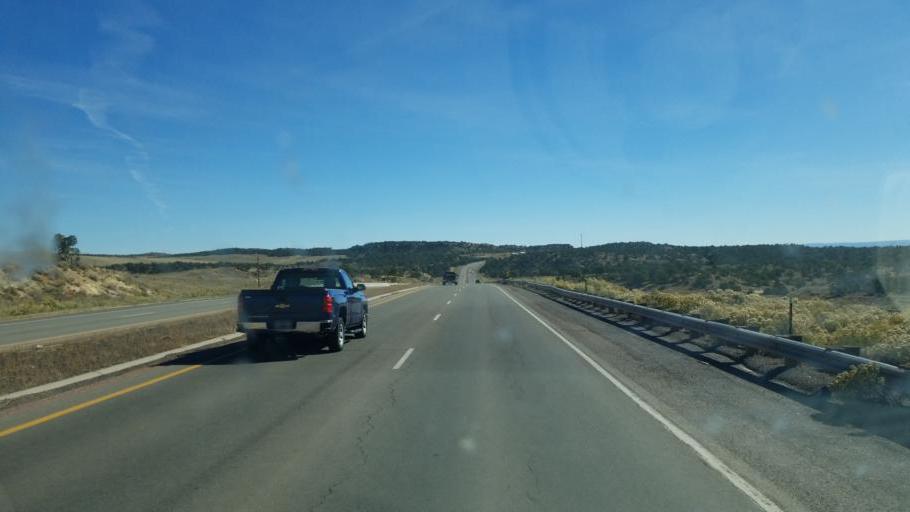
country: US
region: Arizona
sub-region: Apache County
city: Window Rock
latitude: 35.6374
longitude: -108.9864
